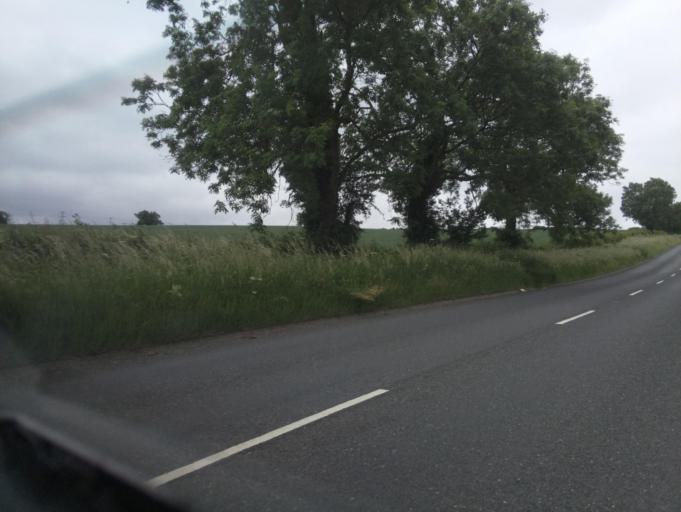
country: GB
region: England
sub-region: District of Rutland
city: Preston
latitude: 52.6203
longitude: -0.7126
